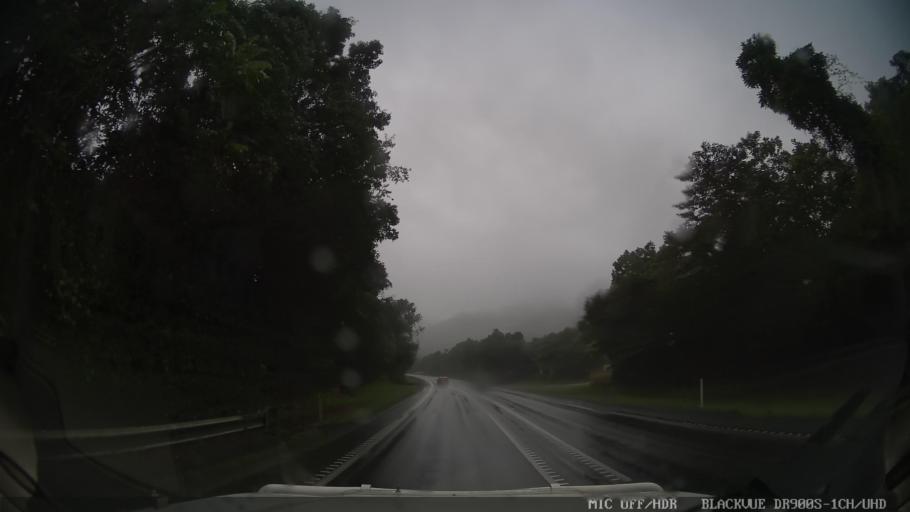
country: AU
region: Queensland
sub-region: Cassowary Coast
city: Innisfail
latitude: -17.8637
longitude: 145.9842
